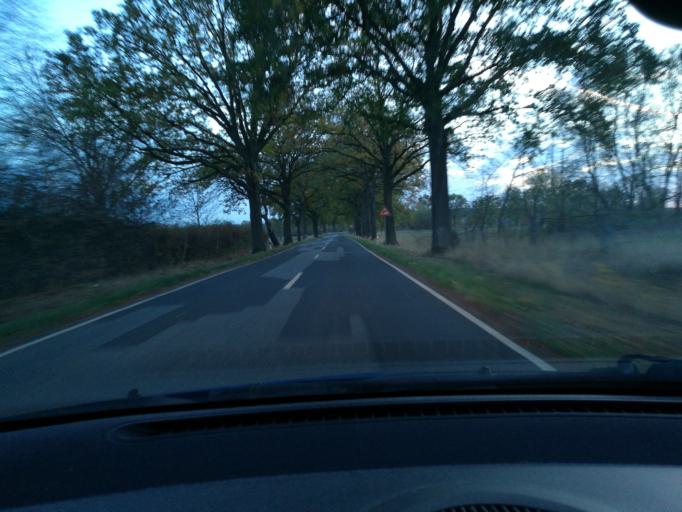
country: DE
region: Brandenburg
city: Lenzen
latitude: 53.0870
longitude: 11.4668
